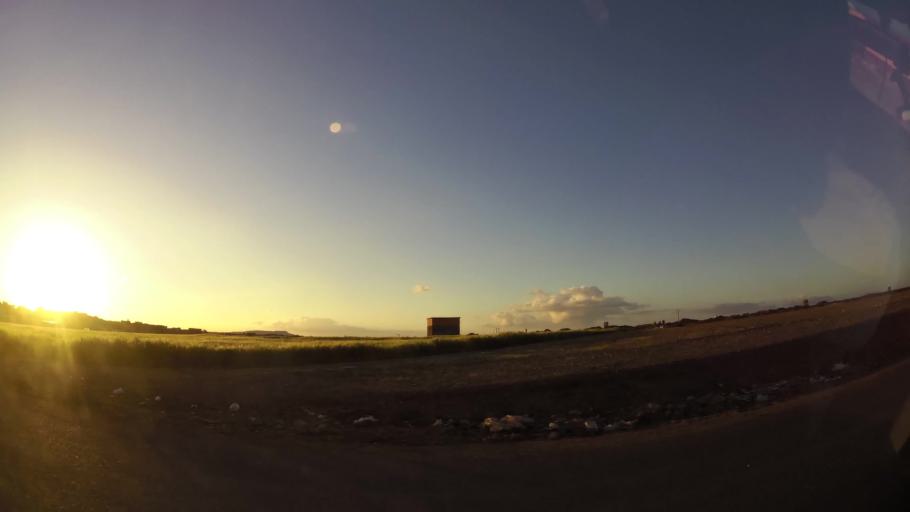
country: MA
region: Marrakech-Tensift-Al Haouz
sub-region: Kelaa-Des-Sraghna
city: Sidi Abdallah
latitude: 32.2404
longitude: -7.9343
